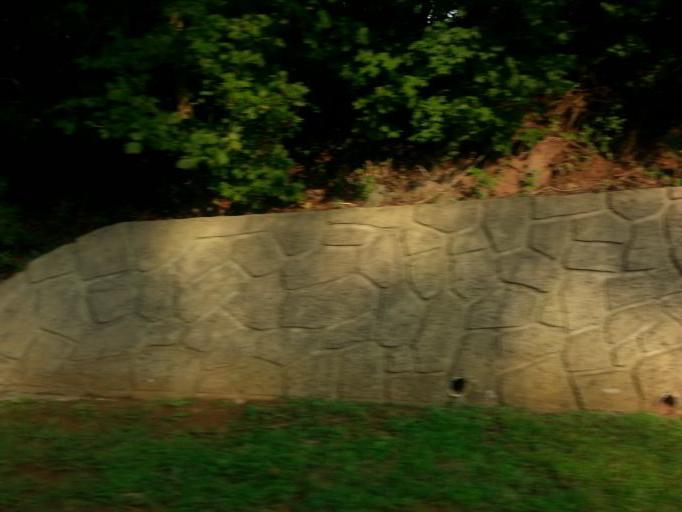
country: US
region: Tennessee
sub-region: Knox County
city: Knoxville
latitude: 35.9087
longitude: -83.9383
